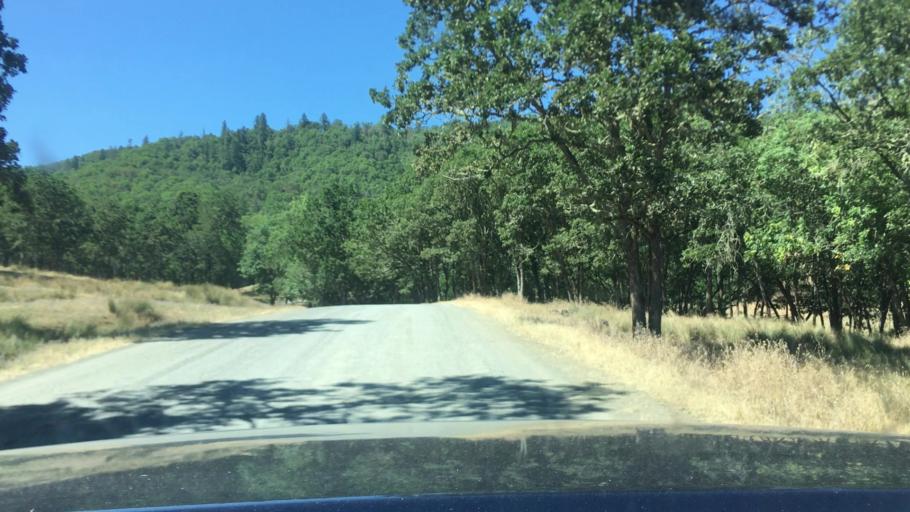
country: US
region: Oregon
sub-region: Douglas County
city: Winston
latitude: 43.1375
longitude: -123.4408
